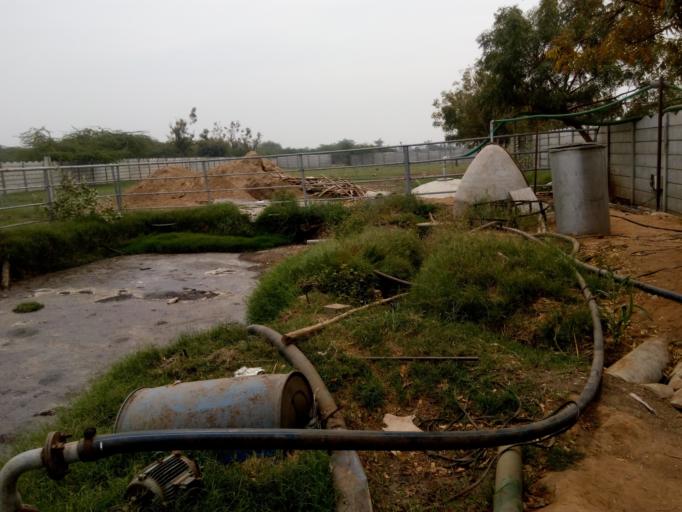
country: IN
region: Gujarat
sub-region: Ahmadabad
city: Sarkhej
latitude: 22.9802
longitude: 72.4758
